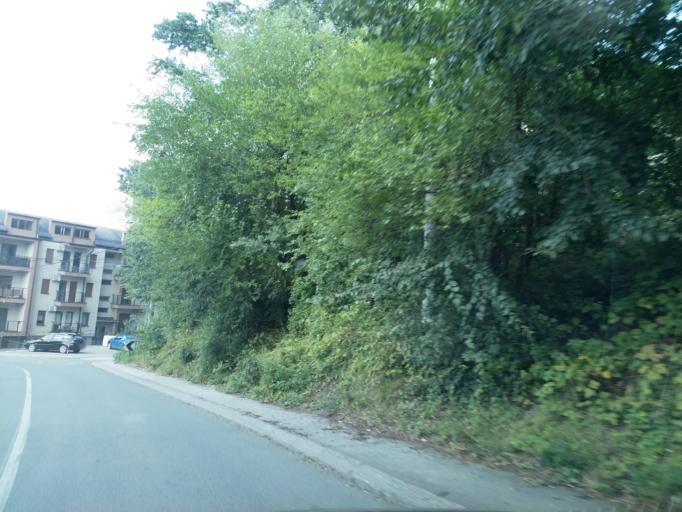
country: RS
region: Central Serbia
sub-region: Raski Okrug
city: Vrnjacka Banja
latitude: 43.6232
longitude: 20.8978
